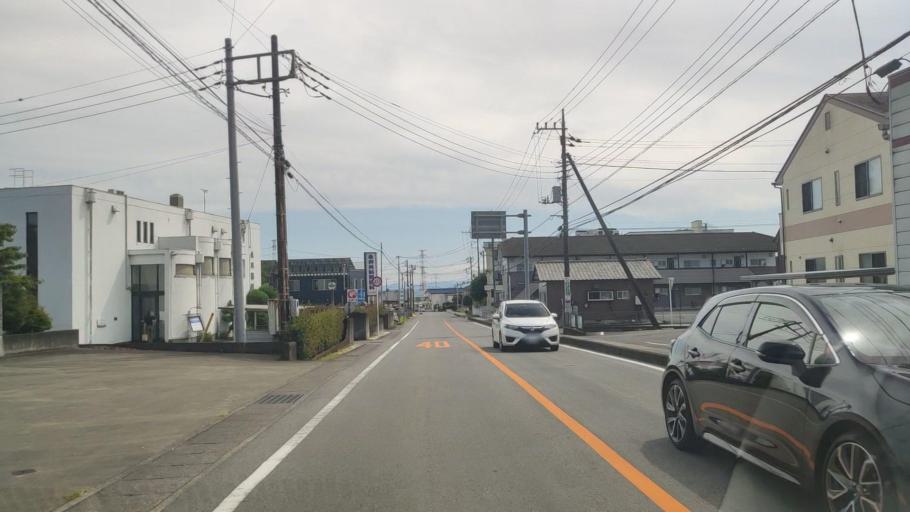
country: JP
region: Gunma
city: Kanekomachi
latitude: 36.3859
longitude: 138.9606
